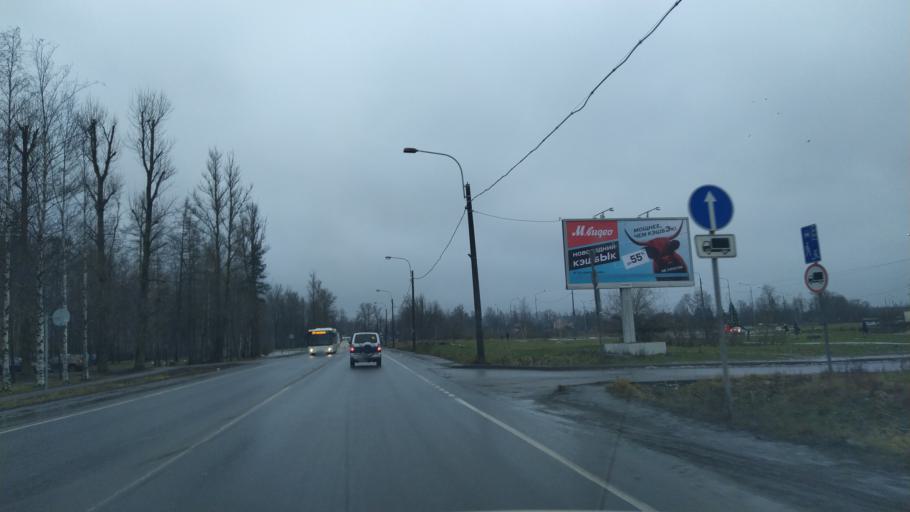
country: RU
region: St.-Petersburg
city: Tyarlevo
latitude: 59.7294
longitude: 30.4628
